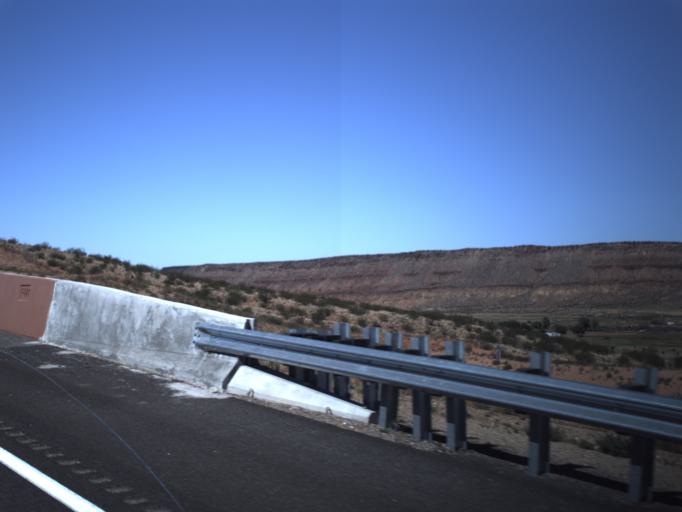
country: US
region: Utah
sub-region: Washington County
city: Washington
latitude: 37.1141
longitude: -113.4518
